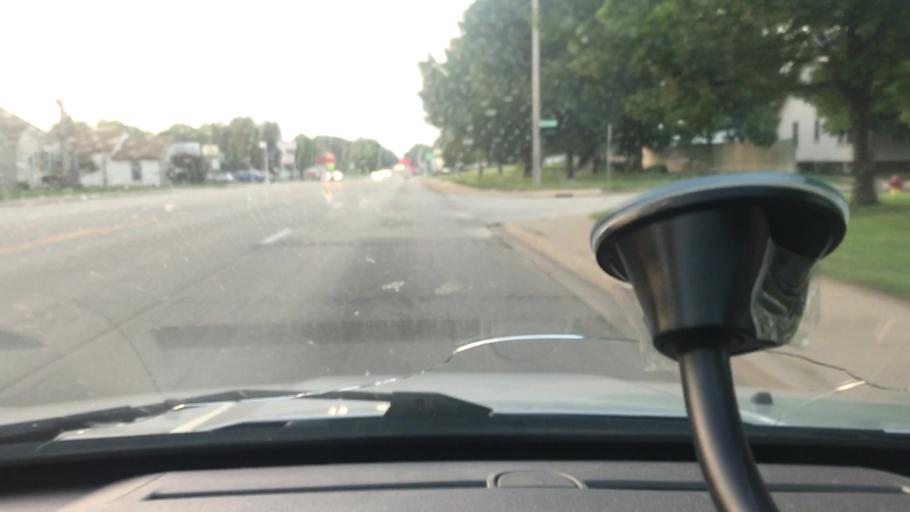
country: US
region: Illinois
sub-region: Tazewell County
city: Pekin
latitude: 40.5761
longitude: -89.6410
